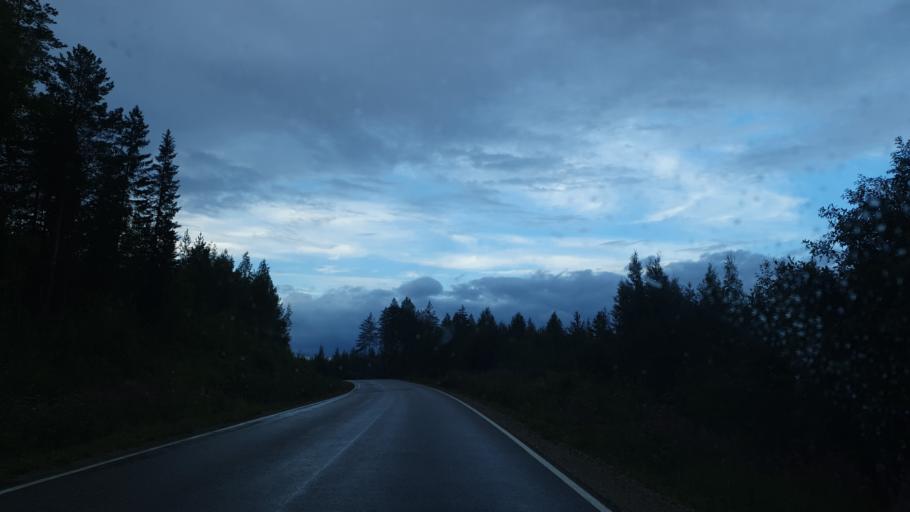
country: FI
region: North Karelia
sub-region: Pielisen Karjala
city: Lieksa
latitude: 63.6260
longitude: 29.8666
